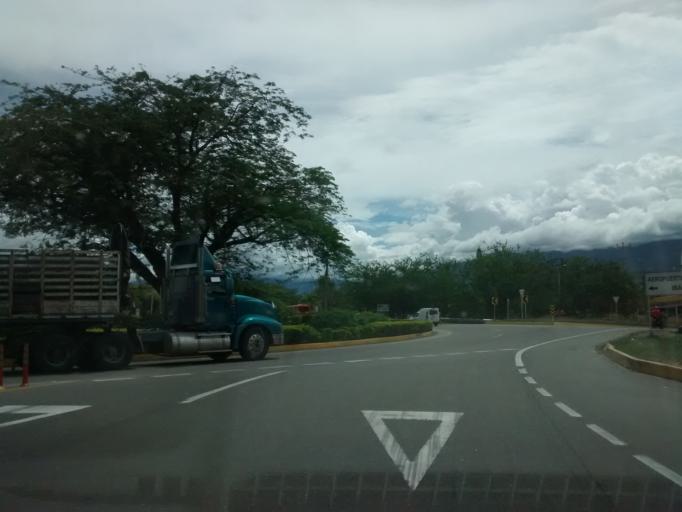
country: CO
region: Tolima
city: Ibague
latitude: 4.4000
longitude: -75.1451
